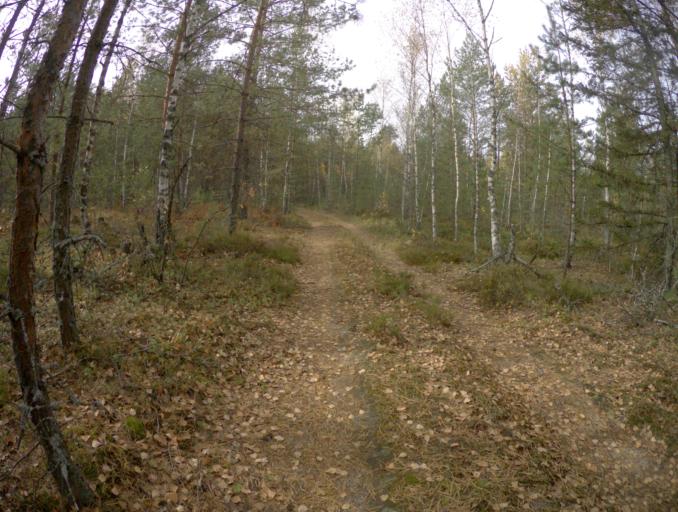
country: RU
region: Vladimir
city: Vorsha
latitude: 55.9712
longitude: 40.1285
